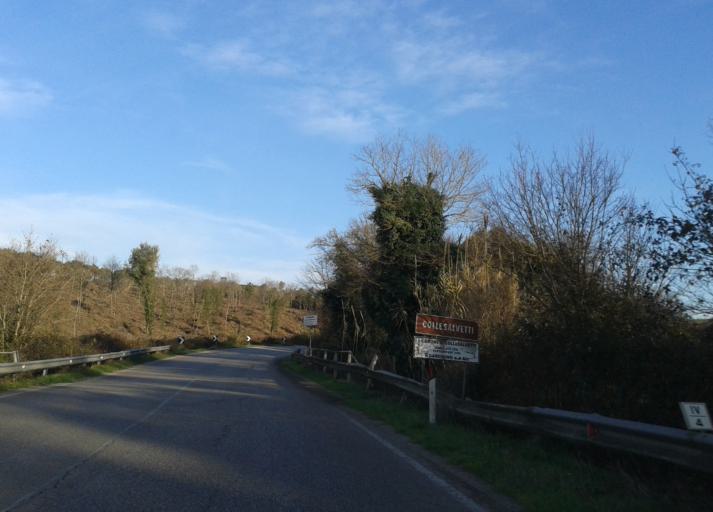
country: IT
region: Tuscany
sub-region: Provincia di Livorno
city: Guasticce
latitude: 43.5665
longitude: 10.3830
